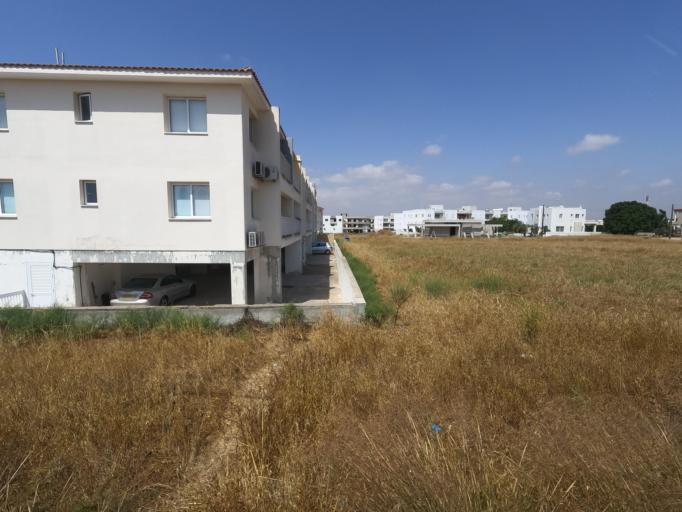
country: CY
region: Ammochostos
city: Paralimni
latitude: 35.0500
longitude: 33.9797
